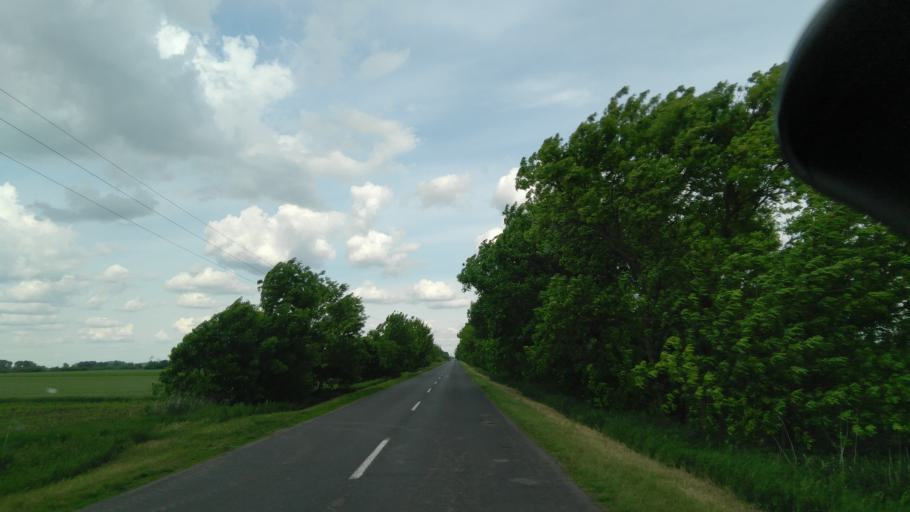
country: RO
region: Arad
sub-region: Comuna Peregu Mare
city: Peregu Mic
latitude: 46.2953
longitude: 20.9676
